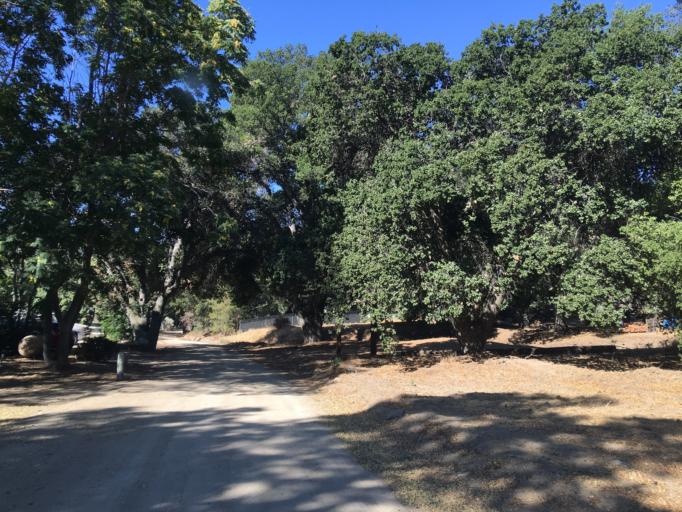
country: US
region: California
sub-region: Los Angeles County
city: Green Valley
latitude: 34.6252
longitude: -118.4088
